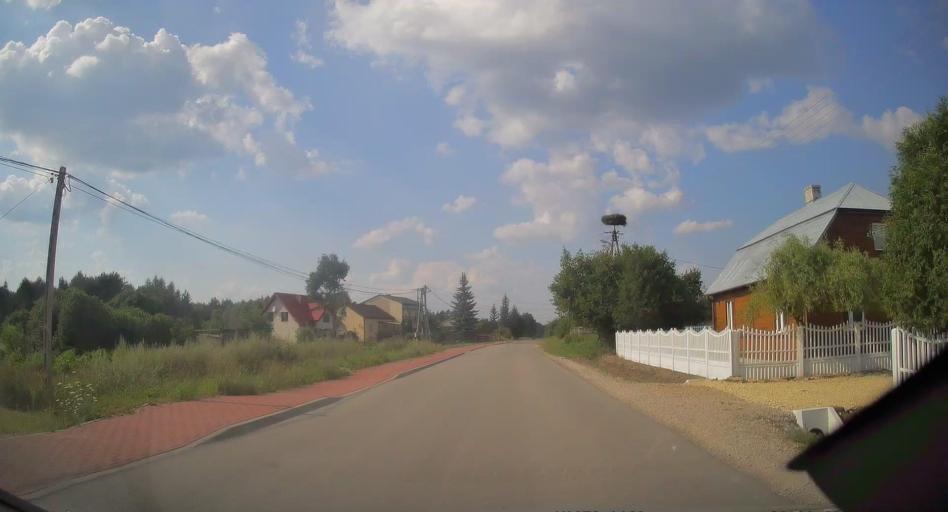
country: PL
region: Swietokrzyskie
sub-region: Powiat konecki
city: Radoszyce
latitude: 51.1156
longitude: 20.2611
